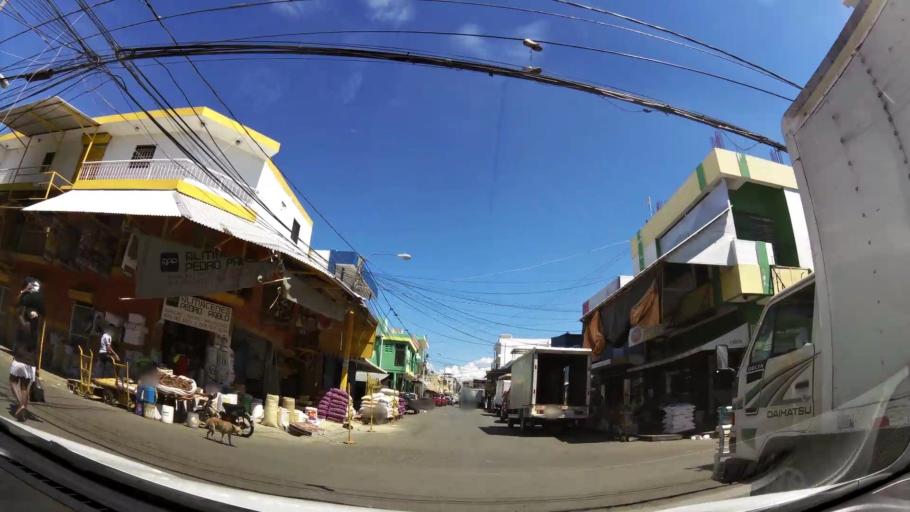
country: DO
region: Santiago
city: Santiago de los Caballeros
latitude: 19.4530
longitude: -70.7111
